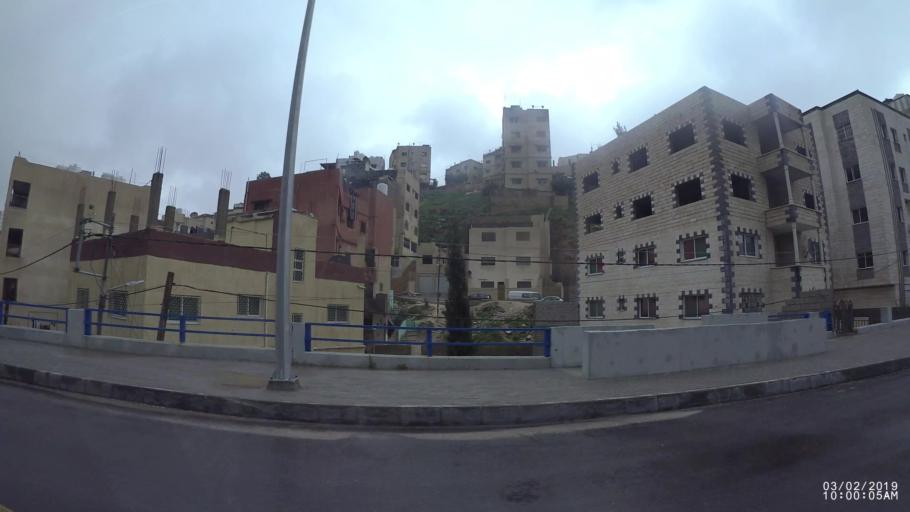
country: JO
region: Amman
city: Amman
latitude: 31.9437
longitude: 35.9067
